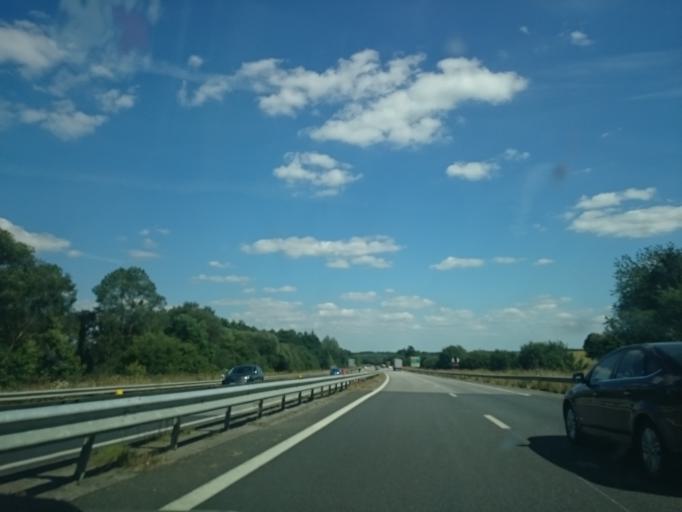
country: FR
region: Brittany
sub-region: Departement des Cotes-d'Armor
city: Loudeac
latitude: 48.1875
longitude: -2.7453
